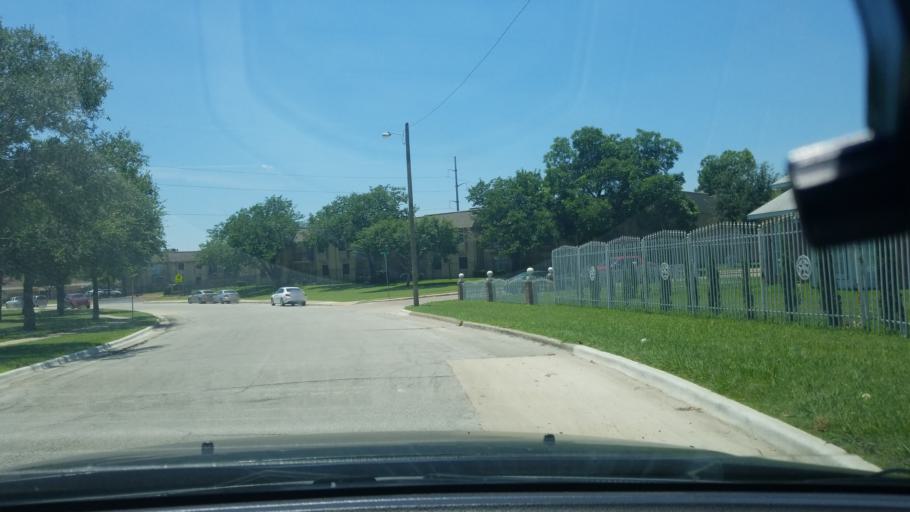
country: US
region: Texas
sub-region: Dallas County
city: Mesquite
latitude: 32.7769
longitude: -96.6108
